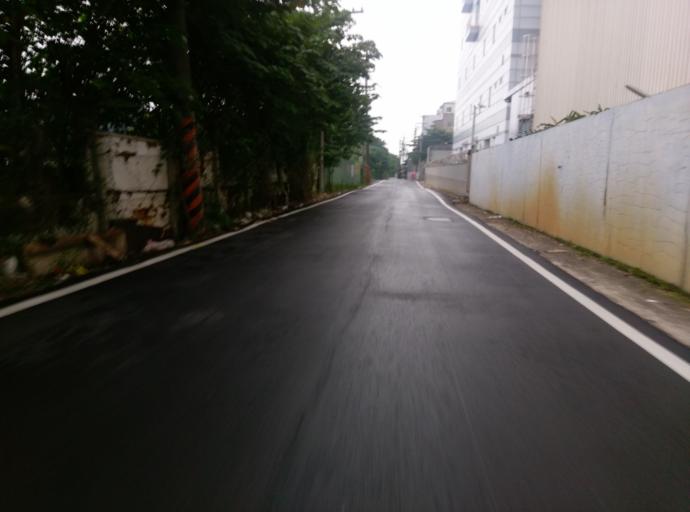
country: TW
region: Taiwan
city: Daxi
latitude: 24.9091
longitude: 121.2408
